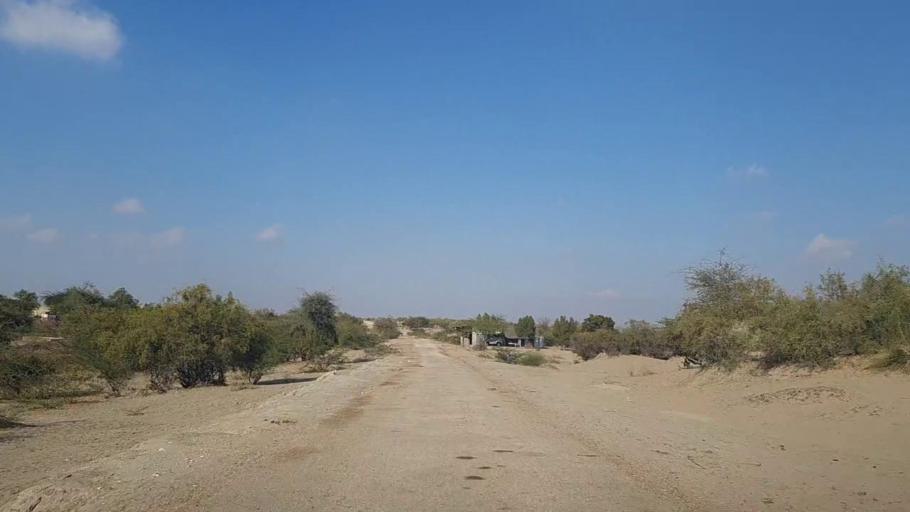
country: PK
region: Sindh
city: Tando Mittha Khan
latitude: 26.0189
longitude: 69.2505
